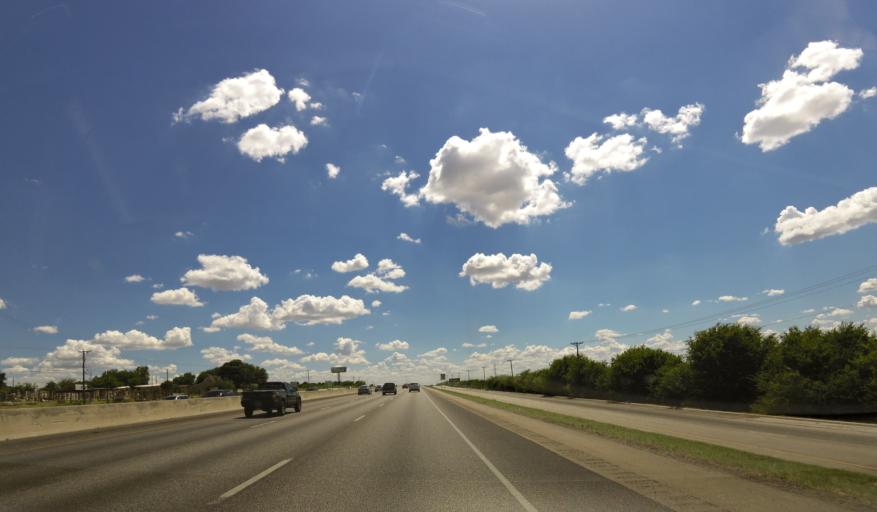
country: US
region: Texas
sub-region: Guadalupe County
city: Northcliff
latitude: 29.6469
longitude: -98.2001
